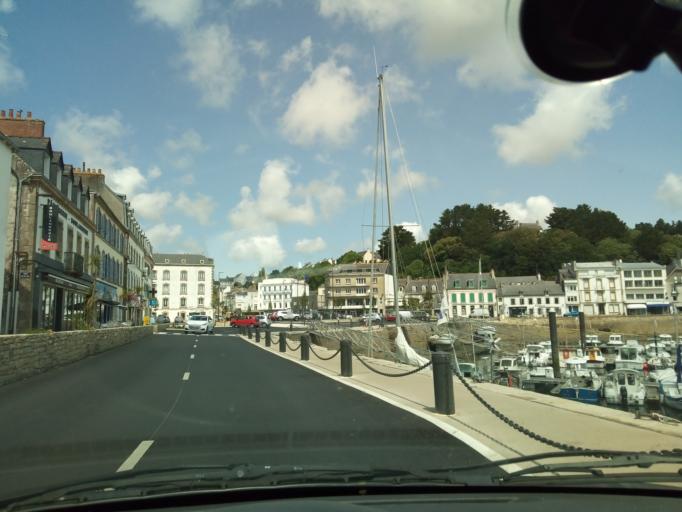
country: FR
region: Brittany
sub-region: Departement du Finistere
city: Audierne
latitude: 48.0222
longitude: -4.5384
